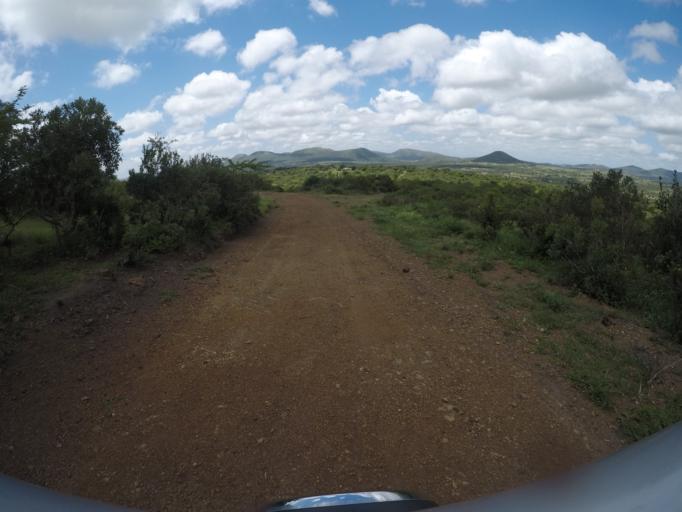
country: ZA
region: KwaZulu-Natal
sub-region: uThungulu District Municipality
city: Empangeni
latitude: -28.5853
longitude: 31.8264
